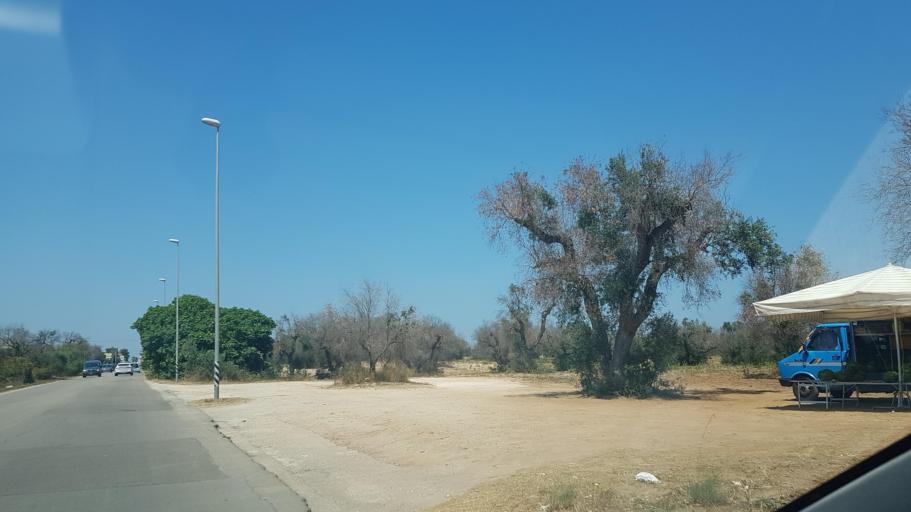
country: IT
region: Apulia
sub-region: Provincia di Lecce
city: Melendugno
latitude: 40.2727
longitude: 18.3440
